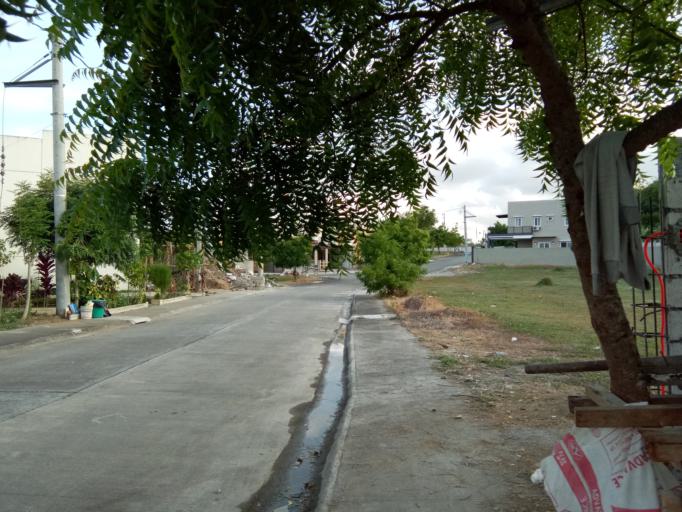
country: PH
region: Calabarzon
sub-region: Province of Cavite
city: Bulihan
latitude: 14.2812
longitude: 120.9729
